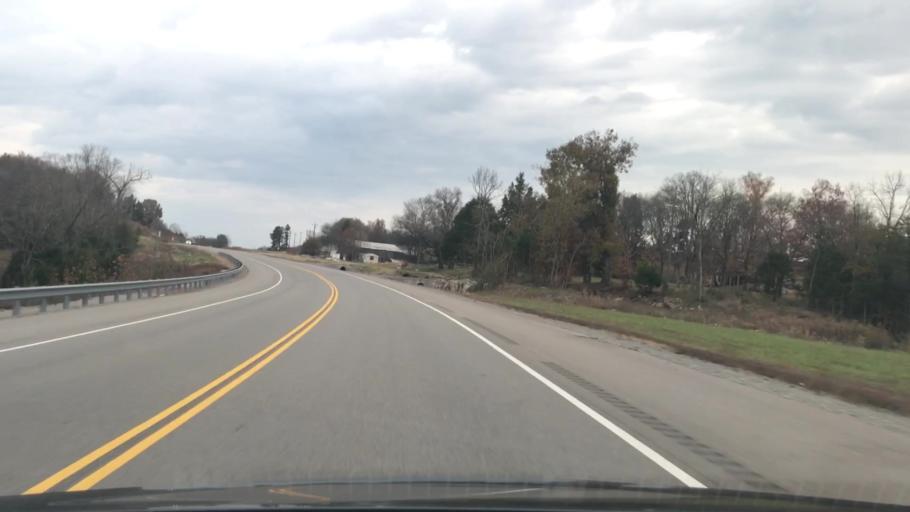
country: US
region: Tennessee
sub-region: Trousdale County
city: Hartsville
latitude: 36.3205
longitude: -86.1762
